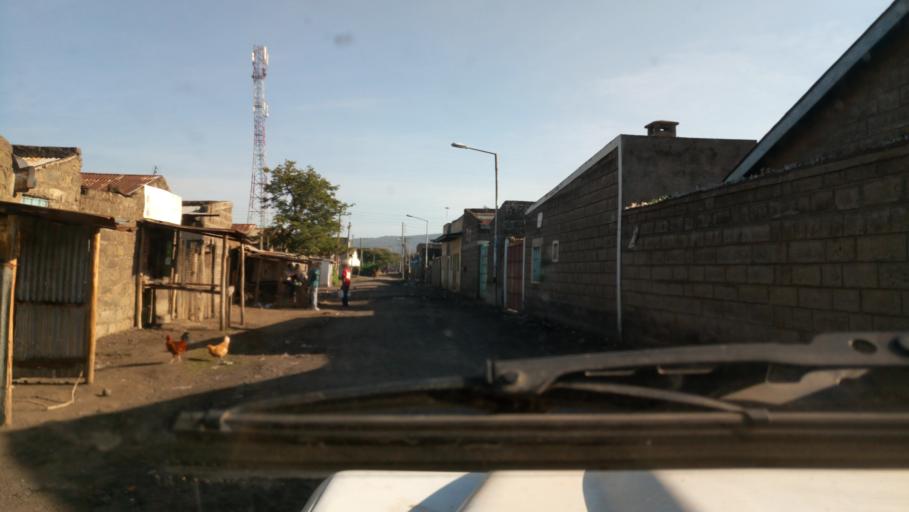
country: KE
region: Nakuru
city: Nakuru
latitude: -0.3055
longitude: 36.0778
